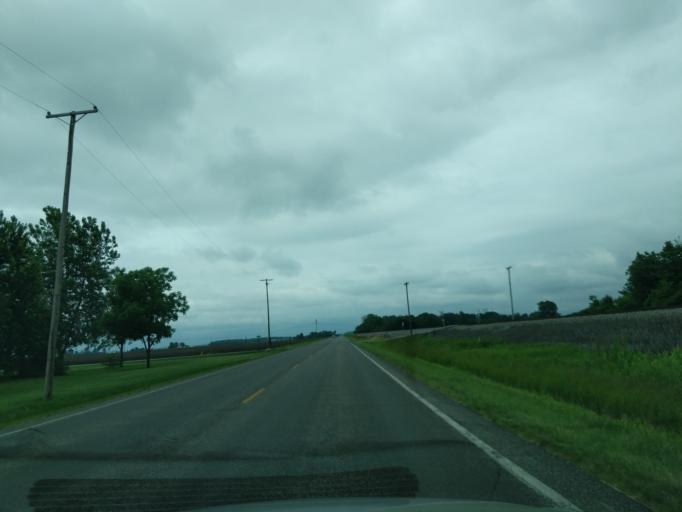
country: US
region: Indiana
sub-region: Madison County
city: Elwood
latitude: 40.2807
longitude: -85.9201
